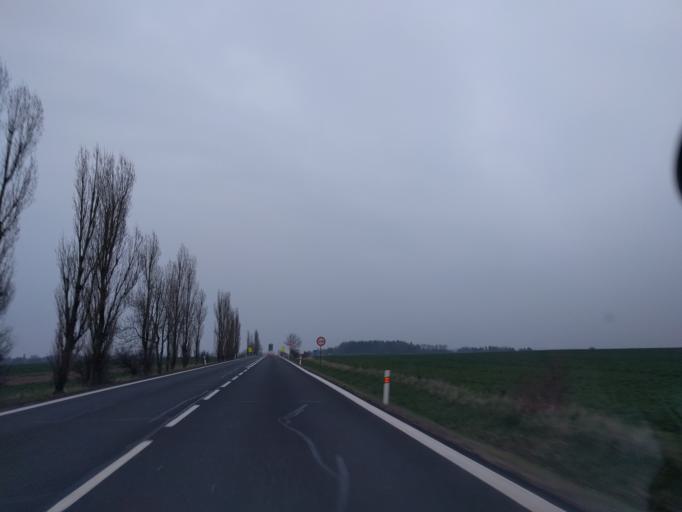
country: CZ
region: Karlovarsky
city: Zlutice
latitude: 50.1350
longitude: 13.2199
